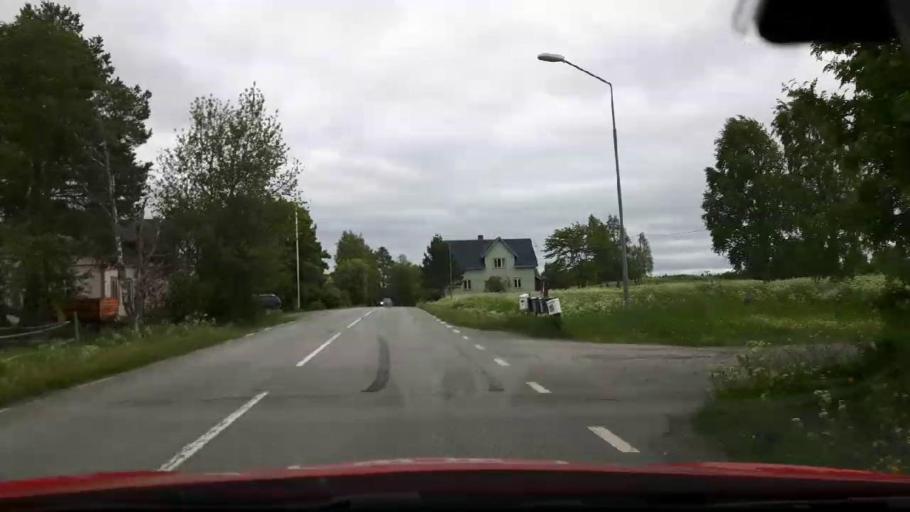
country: SE
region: Jaemtland
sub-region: Stroemsunds Kommun
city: Stroemsund
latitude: 63.5554
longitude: 15.4031
